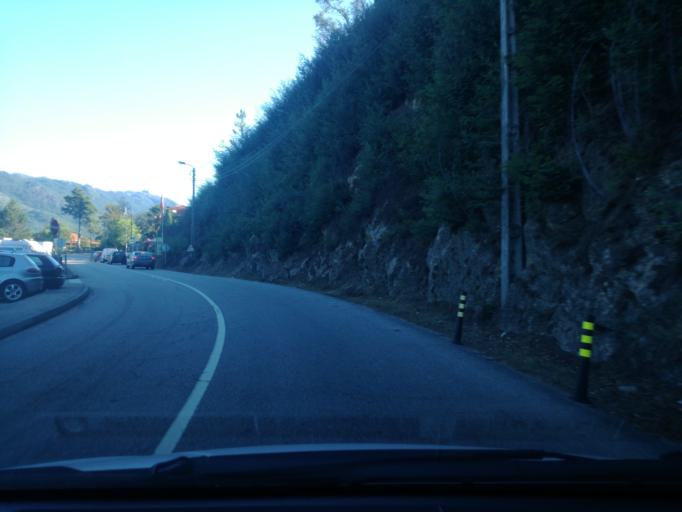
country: PT
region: Braga
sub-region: Vieira do Minho
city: Real
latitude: 41.6776
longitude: -8.1761
